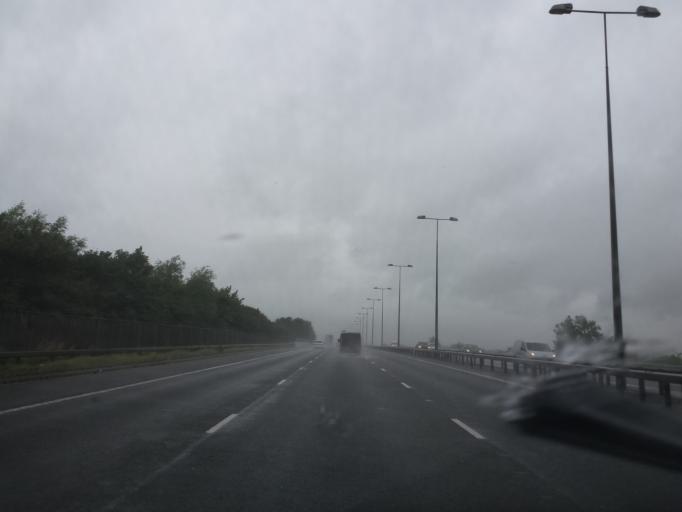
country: GB
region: England
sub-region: Derbyshire
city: Long Eaton
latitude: 52.8894
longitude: -1.3037
